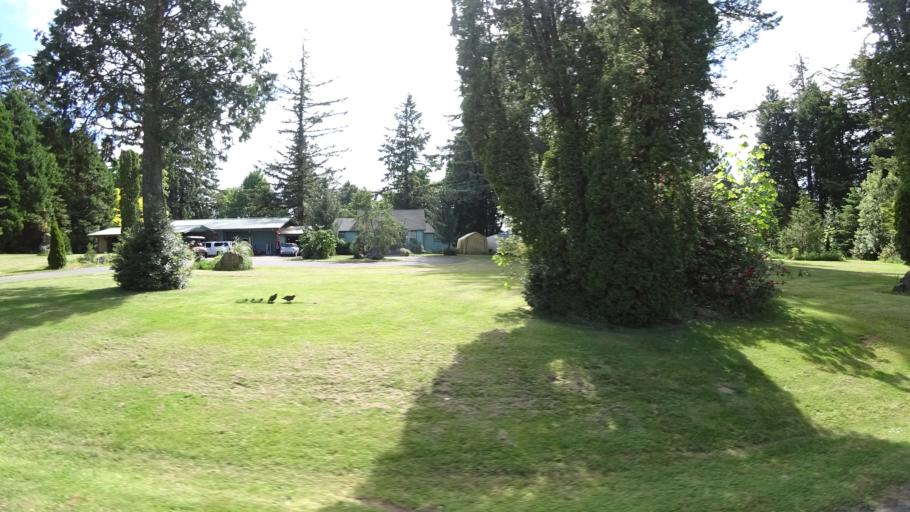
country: US
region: Oregon
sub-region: Washington County
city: Cedar Mill
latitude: 45.5785
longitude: -122.7956
